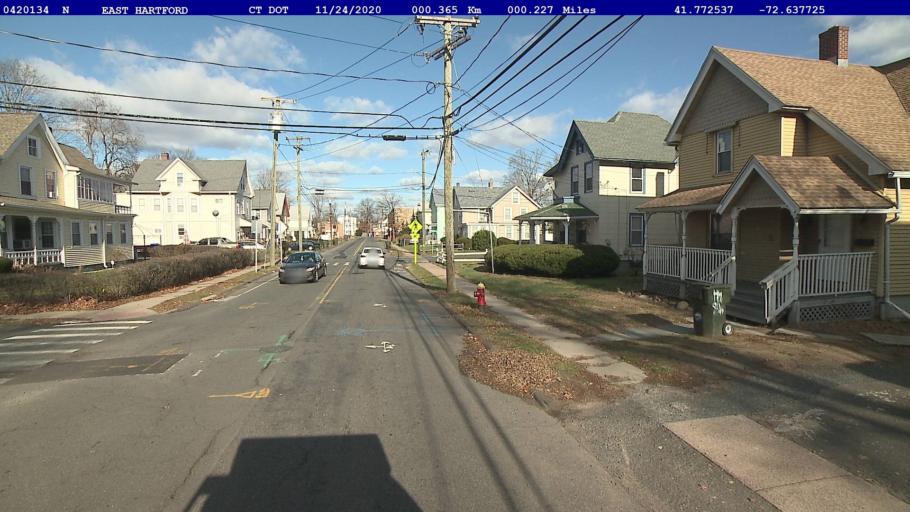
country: US
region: Connecticut
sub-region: Hartford County
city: East Hartford
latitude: 41.7725
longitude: -72.6377
